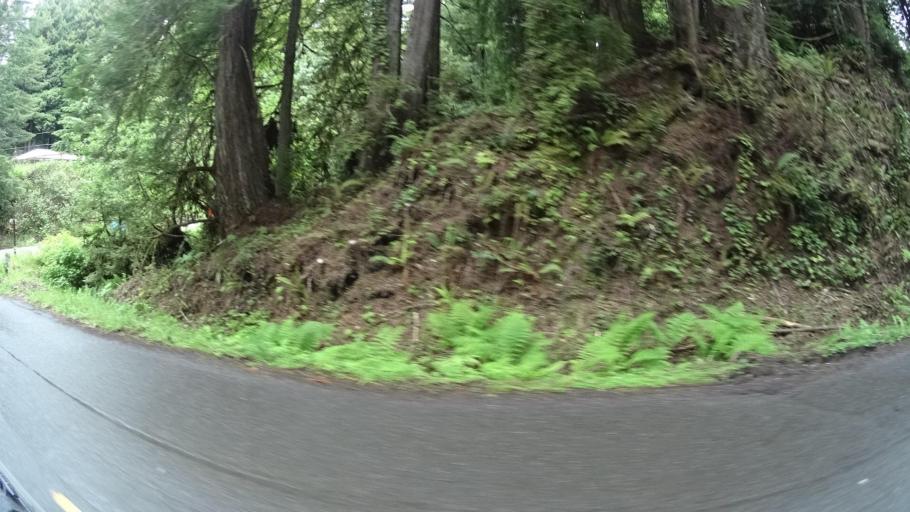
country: US
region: California
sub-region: Humboldt County
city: Bayside
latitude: 40.8270
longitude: -124.0371
